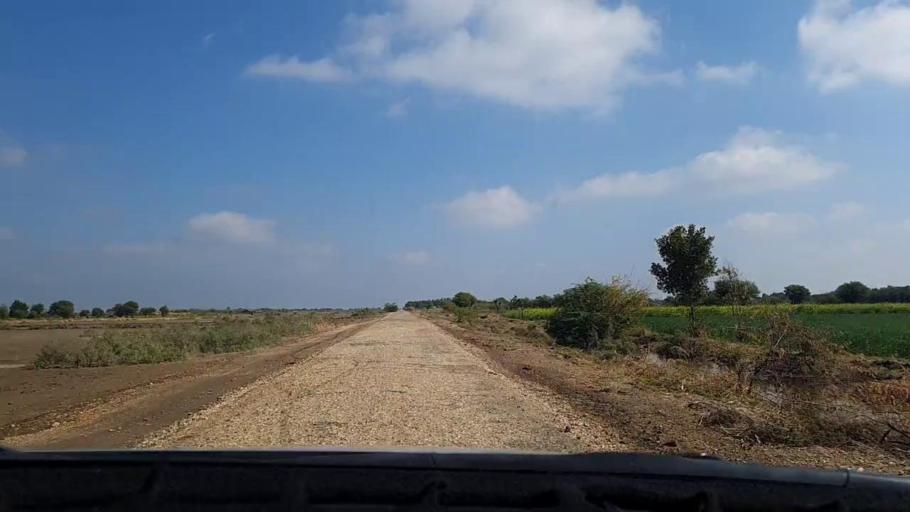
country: PK
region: Sindh
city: Pithoro
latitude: 25.7371
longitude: 69.2525
